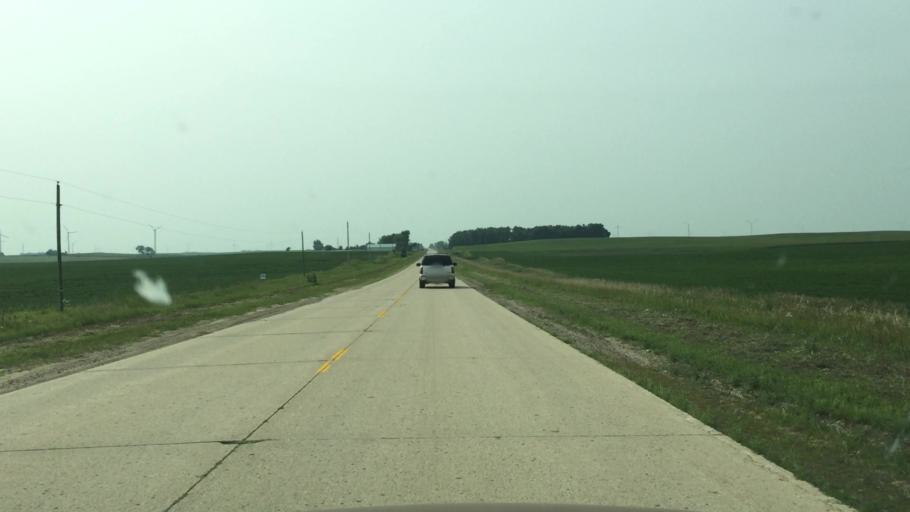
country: US
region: Iowa
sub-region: Dickinson County
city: Lake Park
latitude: 43.4278
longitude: -95.2891
